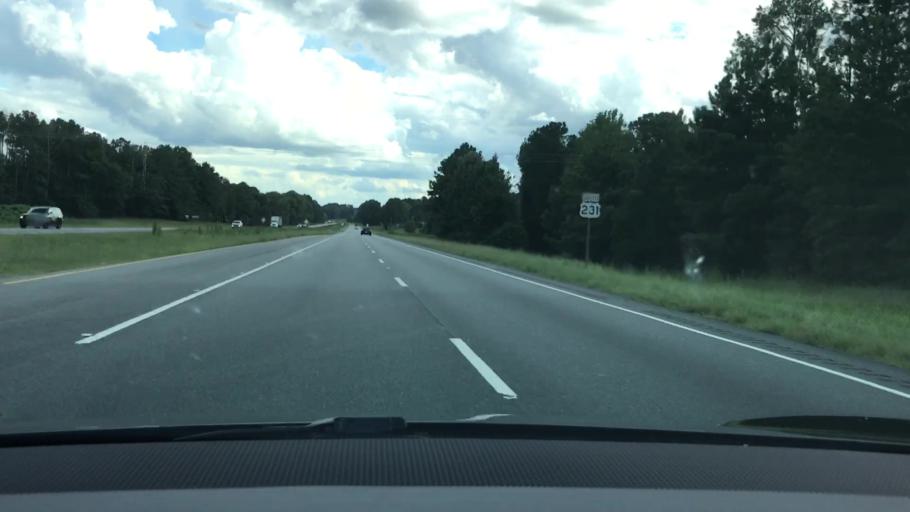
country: US
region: Alabama
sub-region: Pike County
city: Troy
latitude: 31.9600
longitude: -86.0255
